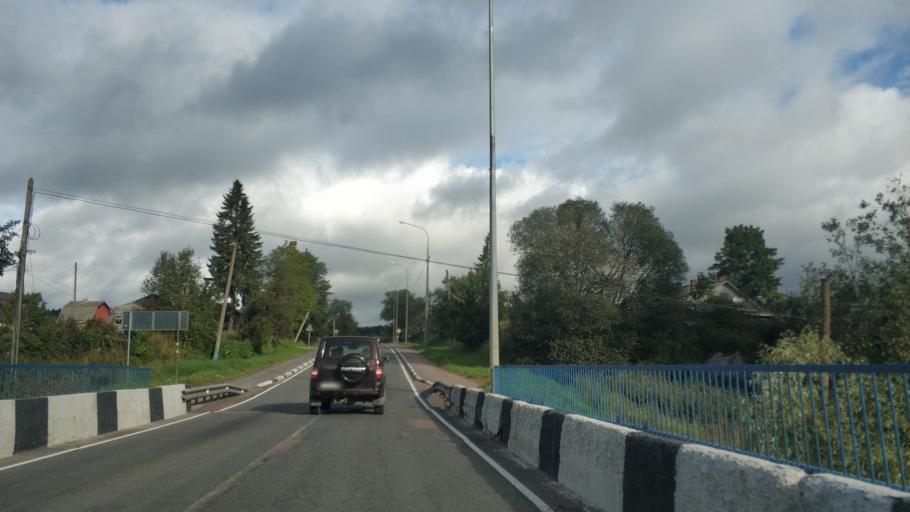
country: RU
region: Republic of Karelia
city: Khelyulya
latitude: 61.7487
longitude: 30.6649
